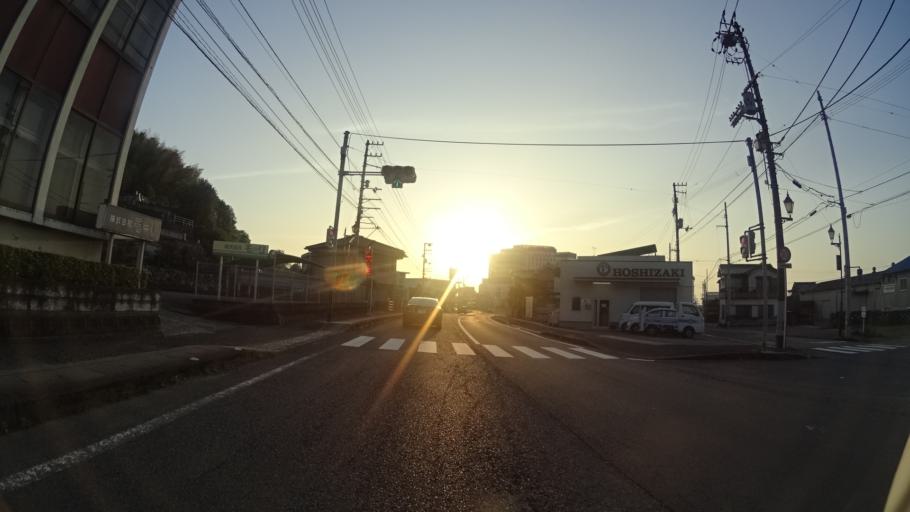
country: JP
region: Ehime
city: Kawanoecho
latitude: 33.9903
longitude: 133.5906
